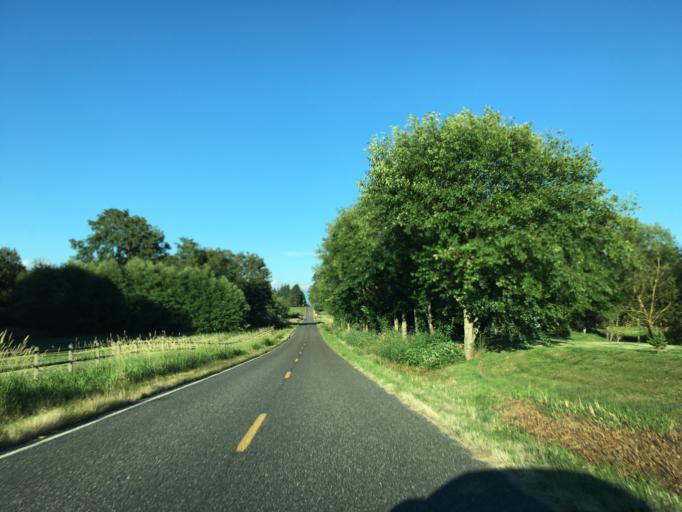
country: US
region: Washington
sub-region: Whatcom County
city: Lynden
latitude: 48.9830
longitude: -122.5259
